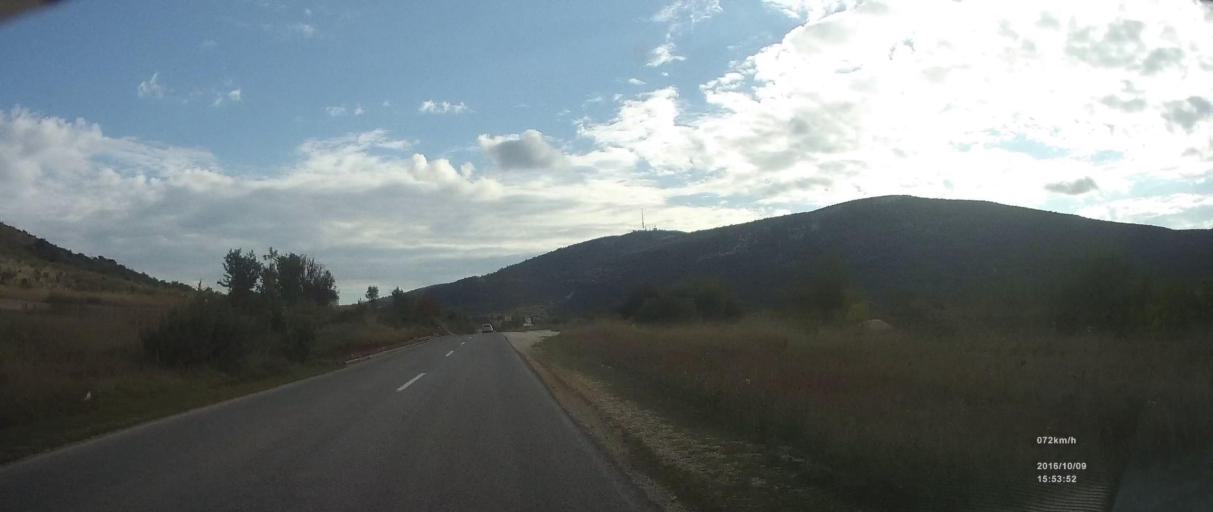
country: HR
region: Splitsko-Dalmatinska
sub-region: Grad Trogir
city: Trogir
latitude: 43.6010
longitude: 16.2248
